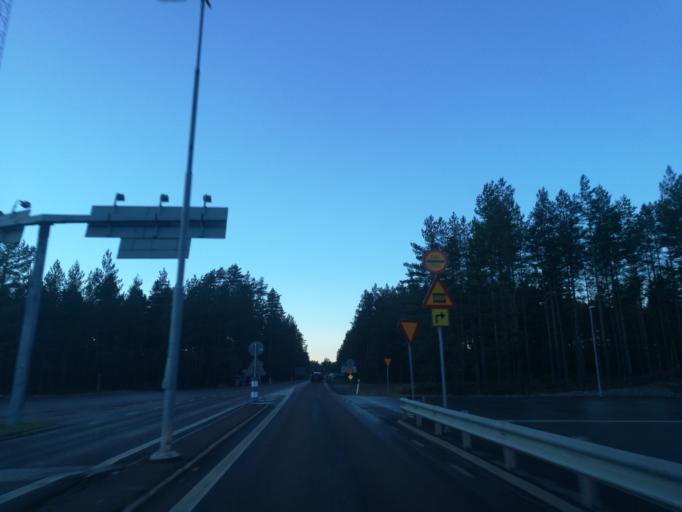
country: SE
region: Vaermland
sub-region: Eda Kommun
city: Charlottenberg
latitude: 59.9274
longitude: 12.2518
